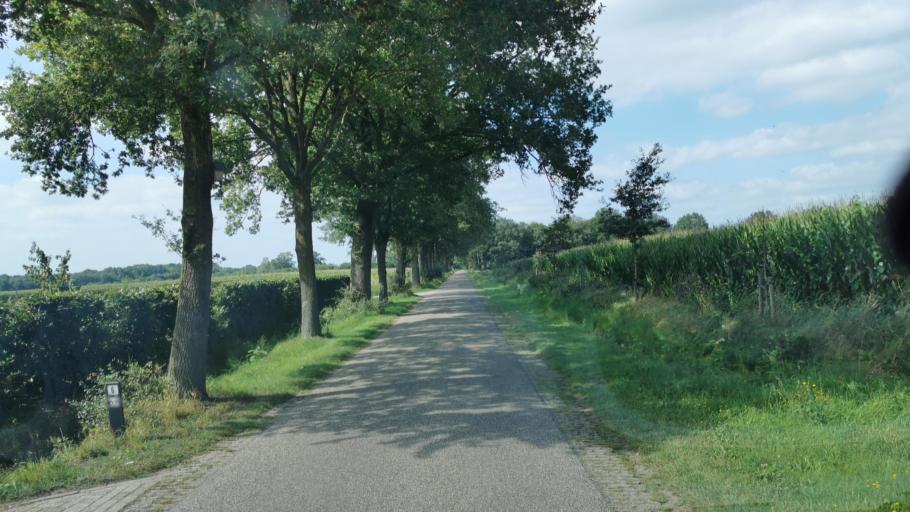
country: NL
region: Overijssel
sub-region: Gemeente Oldenzaal
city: Oldenzaal
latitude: 52.3326
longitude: 6.8833
